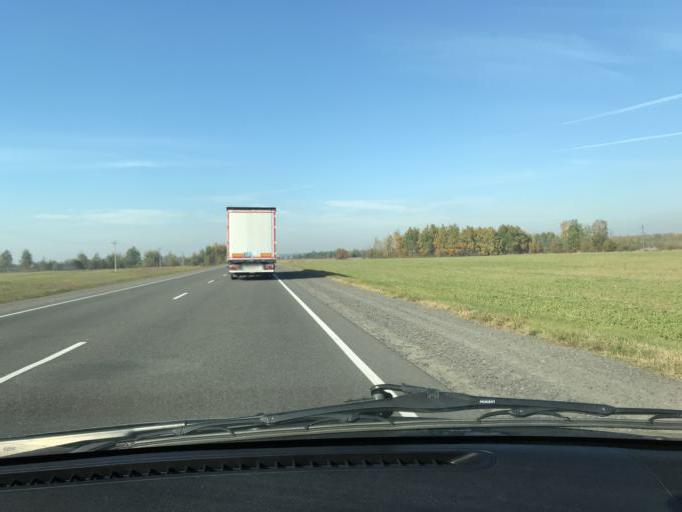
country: BY
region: Brest
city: Horad Luninyets
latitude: 52.3150
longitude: 26.6437
